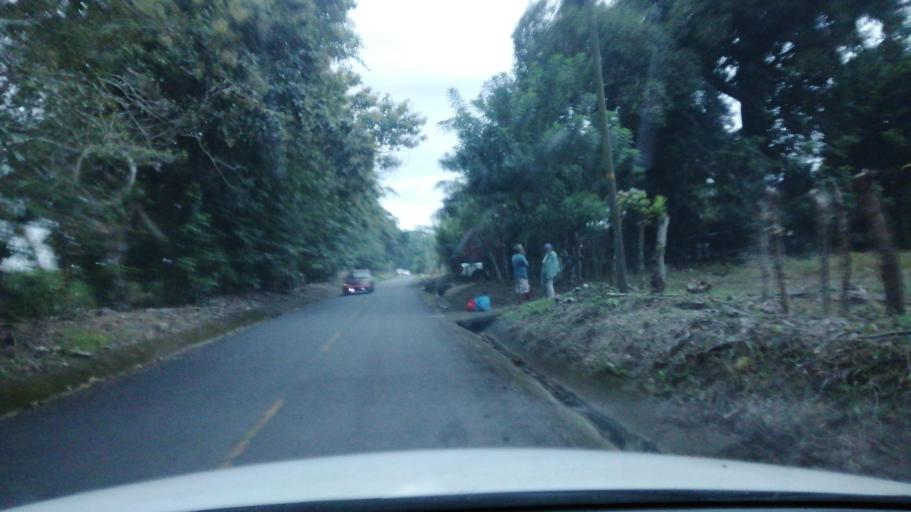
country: PA
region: Chiriqui
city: Alanje
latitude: 8.3999
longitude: -82.4980
